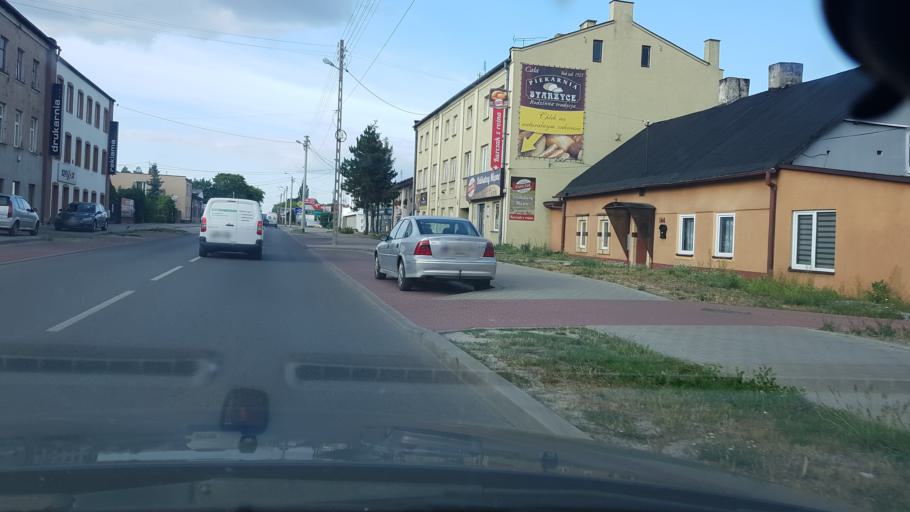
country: PL
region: Lodz Voivodeship
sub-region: Powiat tomaszowski
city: Tomaszow Mazowiecki
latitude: 51.5519
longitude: 20.0169
